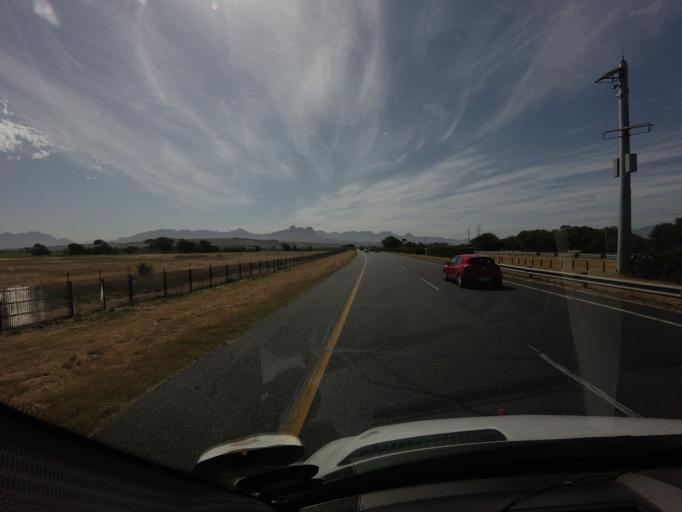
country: ZA
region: Western Cape
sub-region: Cape Winelands District Municipality
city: Stellenbosch
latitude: -34.0427
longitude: 18.7341
